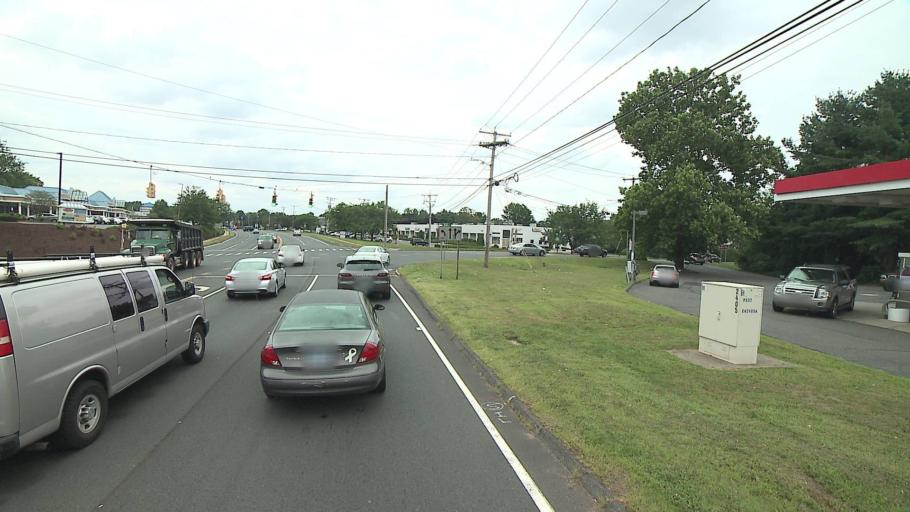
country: US
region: Connecticut
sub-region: Hartford County
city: Newington
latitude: 41.6578
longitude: -72.6784
